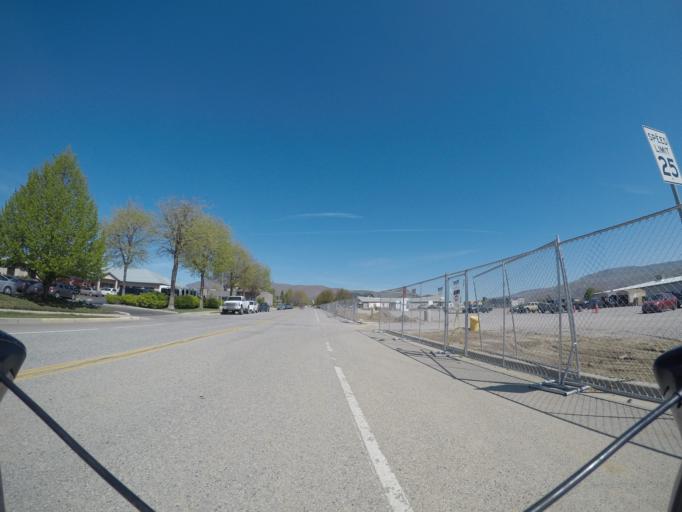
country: US
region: Washington
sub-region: Chelan County
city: Sunnyslope
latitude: 47.4628
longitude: -120.3340
